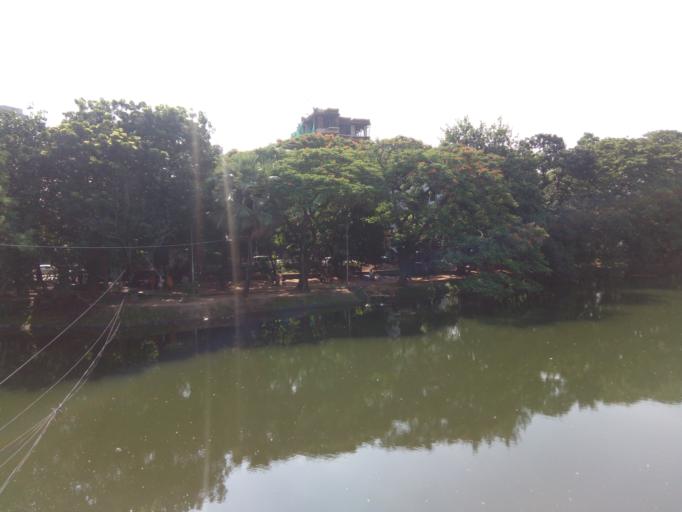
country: BD
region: Dhaka
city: Azimpur
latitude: 23.7459
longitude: 90.3776
